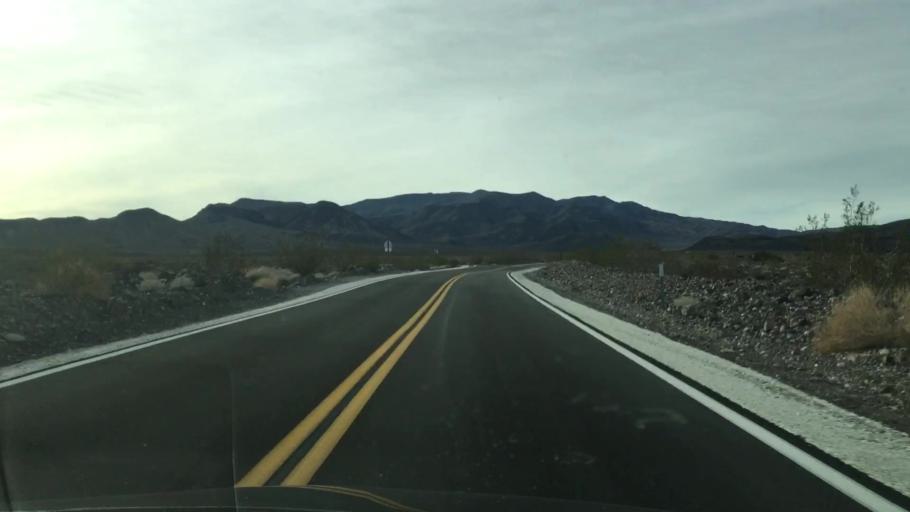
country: US
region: Nevada
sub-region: Nye County
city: Beatty
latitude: 36.4961
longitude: -117.2270
